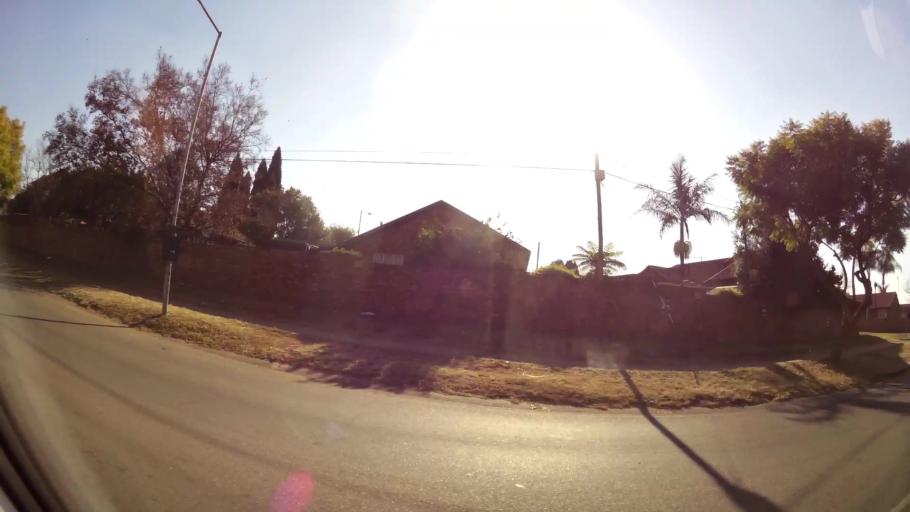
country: ZA
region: Gauteng
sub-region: City of Tshwane Metropolitan Municipality
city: Centurion
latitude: -25.8071
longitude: 28.3010
